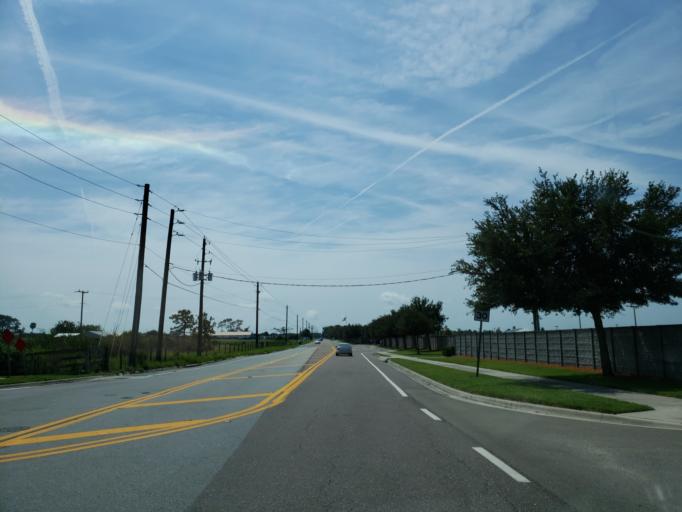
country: US
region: Florida
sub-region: Hillsborough County
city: Riverview
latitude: 27.8462
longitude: -82.3433
